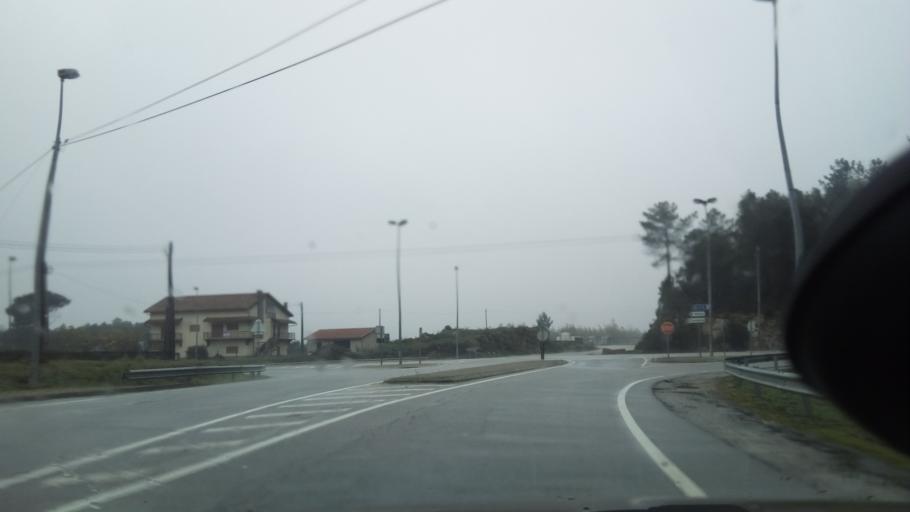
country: PT
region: Viseu
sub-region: Mangualde
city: Mangualde
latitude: 40.6047
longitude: -7.7824
